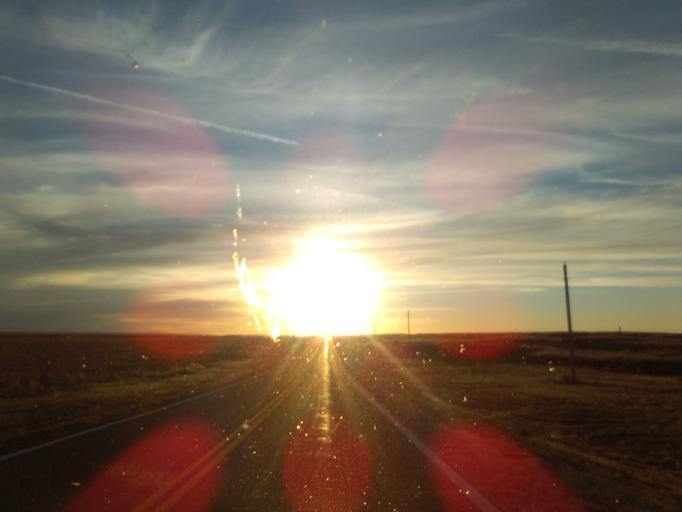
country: US
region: Kansas
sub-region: Wallace County
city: Sharon Springs
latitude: 38.9757
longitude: -101.4384
